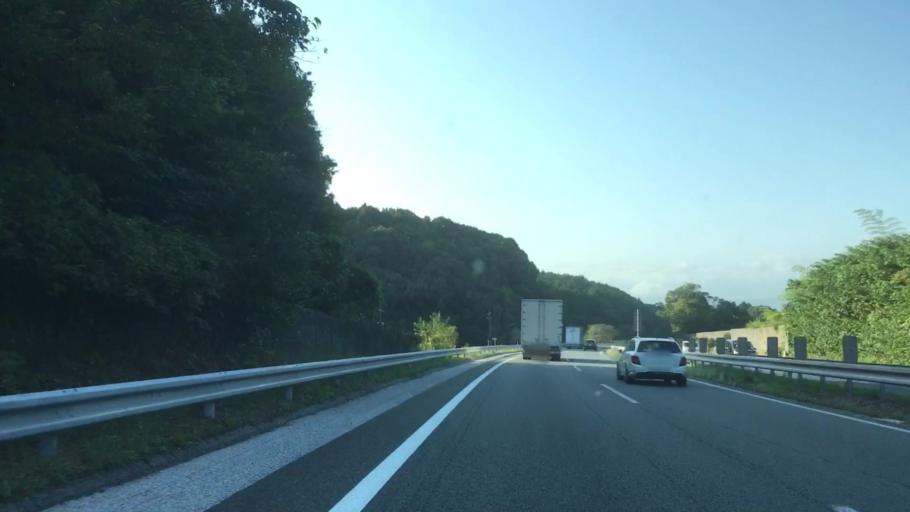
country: JP
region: Yamaguchi
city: Ogori-shimogo
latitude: 34.1460
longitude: 131.3456
